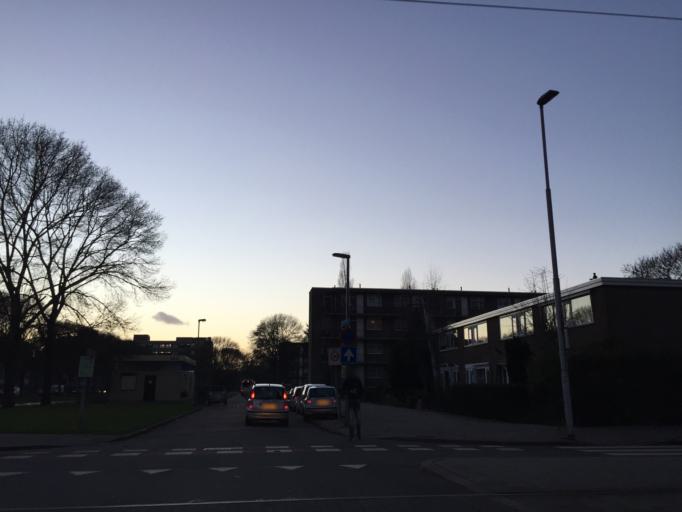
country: NL
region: South Holland
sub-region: Gemeente Rotterdam
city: Rotterdam
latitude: 51.9545
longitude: 4.4683
